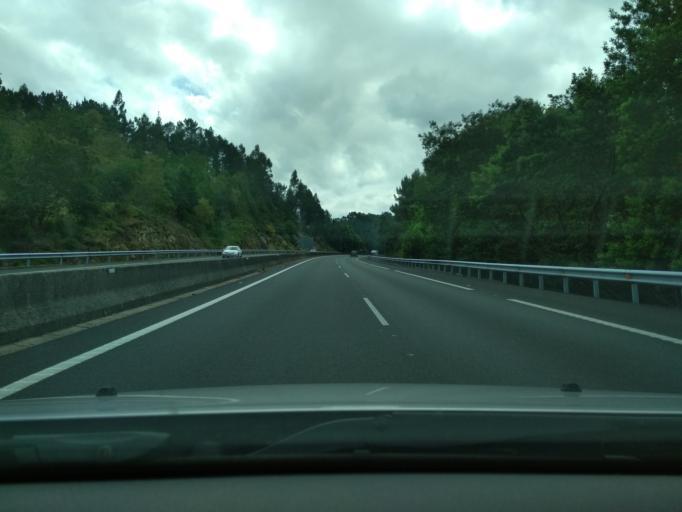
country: ES
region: Galicia
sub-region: Provincia de Pontevedra
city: Portas
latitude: 42.5808
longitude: -8.6748
